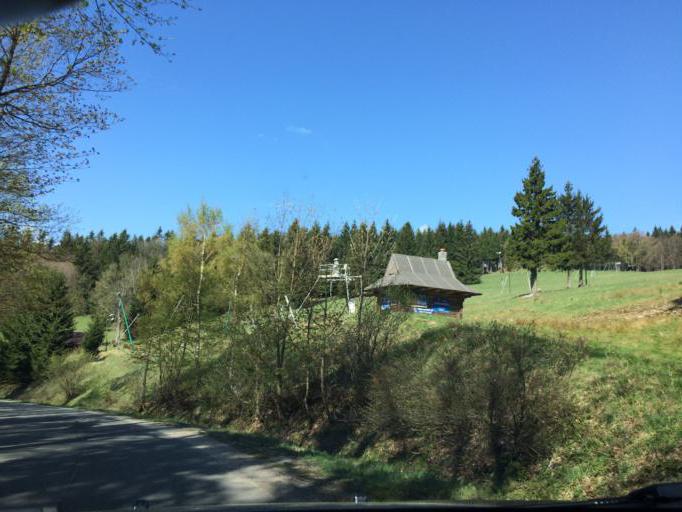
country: PL
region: Lower Silesian Voivodeship
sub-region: Powiat klodzki
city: Jugow
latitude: 50.6551
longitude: 16.5222
